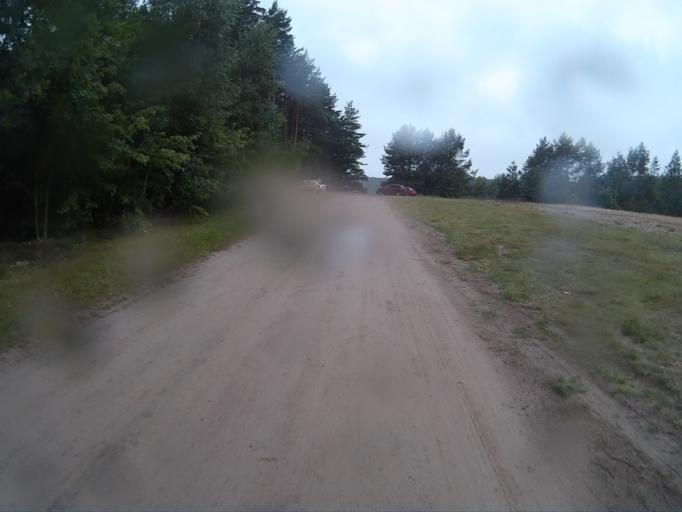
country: PL
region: Kujawsko-Pomorskie
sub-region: Powiat tucholski
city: Gostycyn
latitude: 53.5146
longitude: 17.8767
